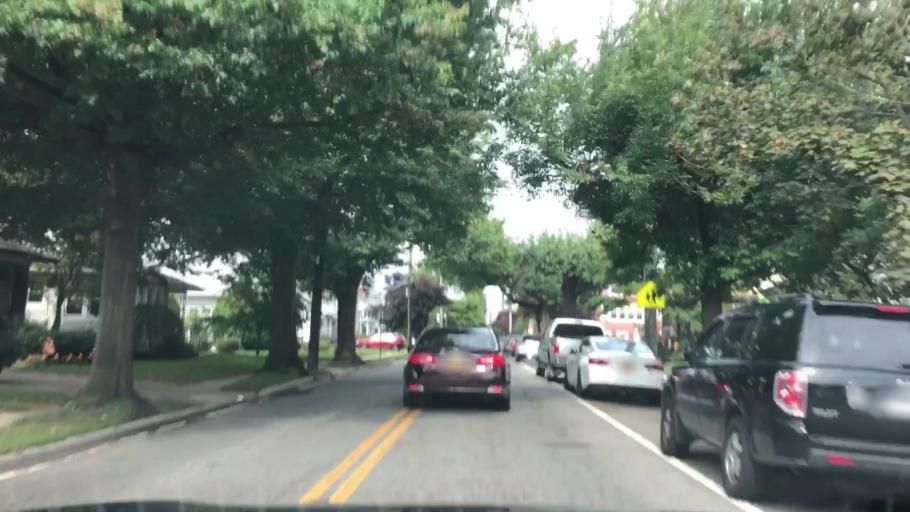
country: US
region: New York
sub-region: Nassau County
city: Floral Park
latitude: 40.7218
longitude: -73.7035
